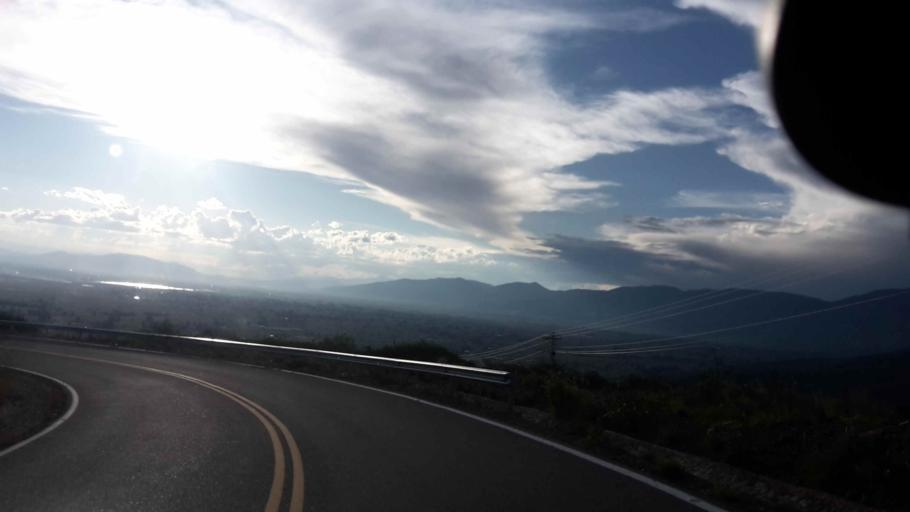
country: BO
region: Cochabamba
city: Arani
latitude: -17.5798
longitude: -65.7473
